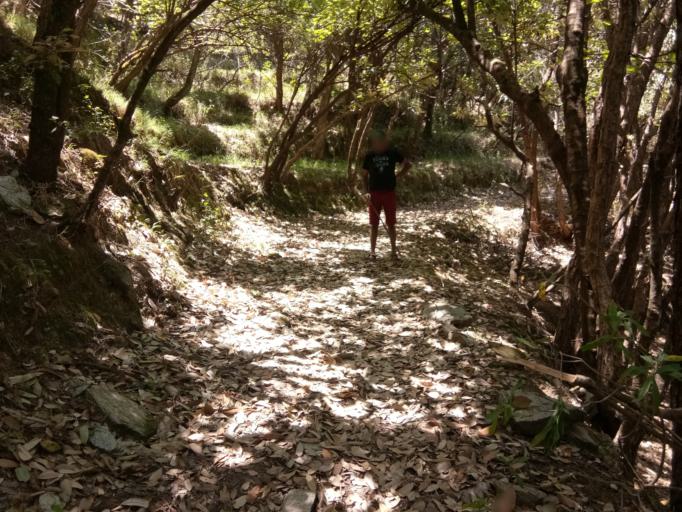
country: IN
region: Uttarakhand
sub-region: Naini Tal
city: Bhim Tal
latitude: 29.3693
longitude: 79.6071
